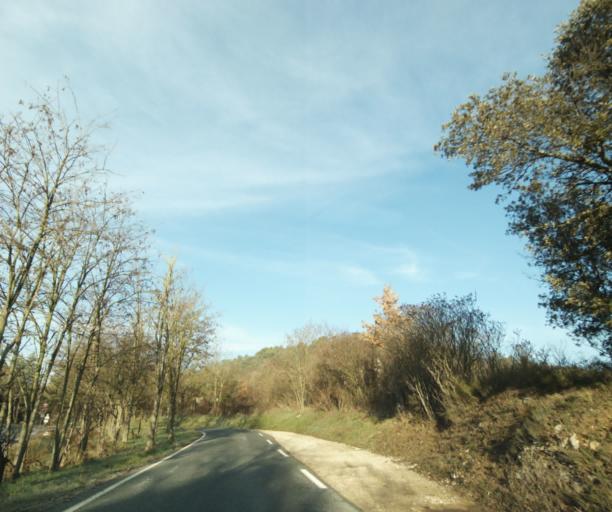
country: FR
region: Provence-Alpes-Cote d'Azur
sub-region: Departement du Var
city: Tourves
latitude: 43.4062
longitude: 5.9354
